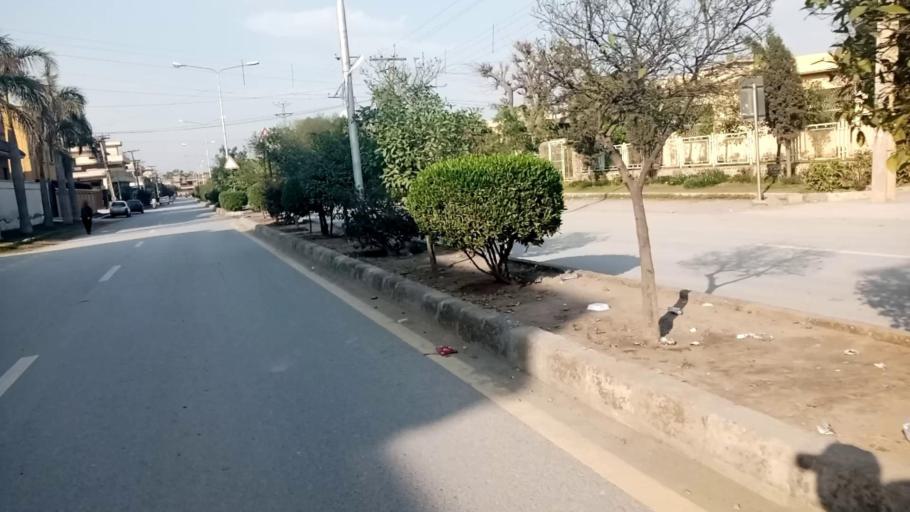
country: PK
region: Khyber Pakhtunkhwa
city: Peshawar
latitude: 33.9907
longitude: 71.4458
